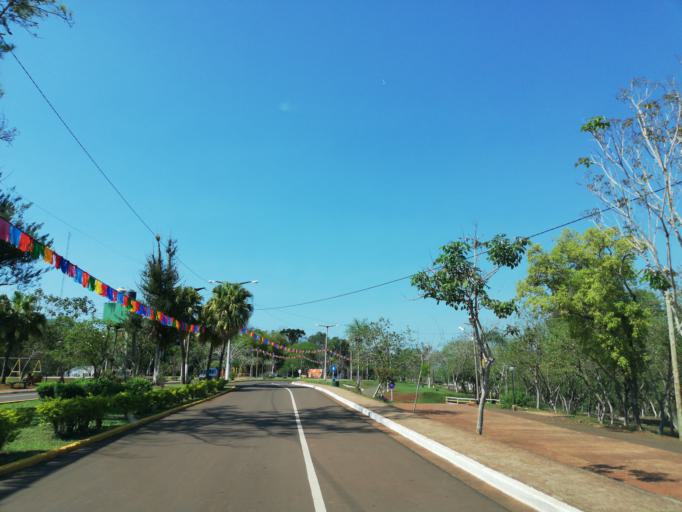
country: AR
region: Misiones
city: Puerto Eldorado
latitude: -26.4109
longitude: -54.6935
